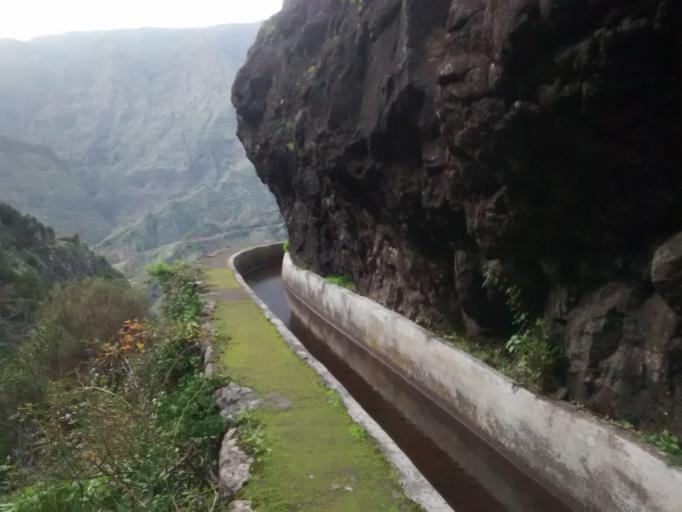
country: PT
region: Madeira
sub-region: Camara de Lobos
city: Curral das Freiras
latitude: 32.7277
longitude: -17.0139
